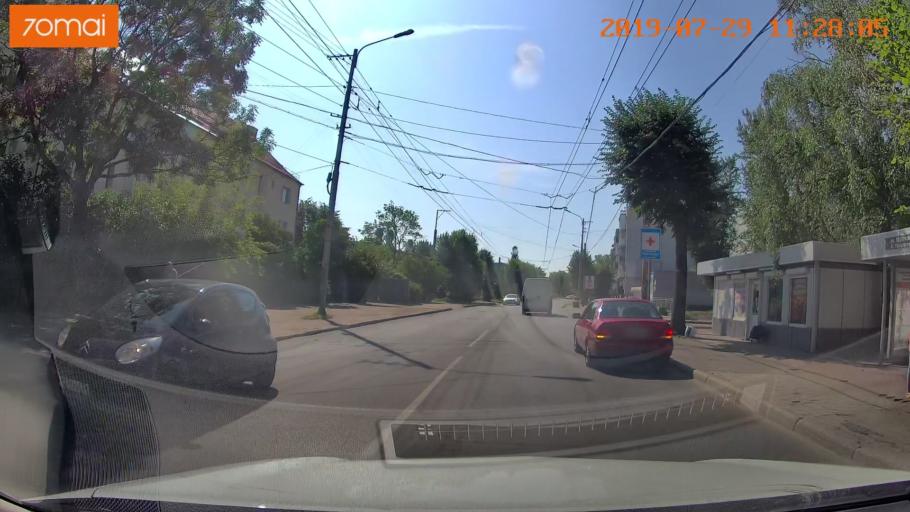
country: RU
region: Kaliningrad
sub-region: Gorod Kaliningrad
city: Kaliningrad
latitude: 54.6888
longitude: 20.5320
